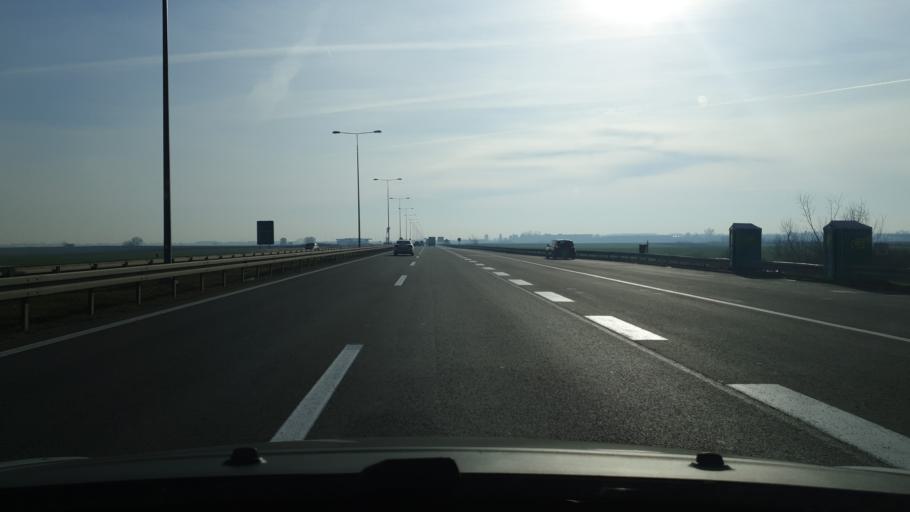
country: RS
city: Dobanovci
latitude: 44.8174
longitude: 20.2528
